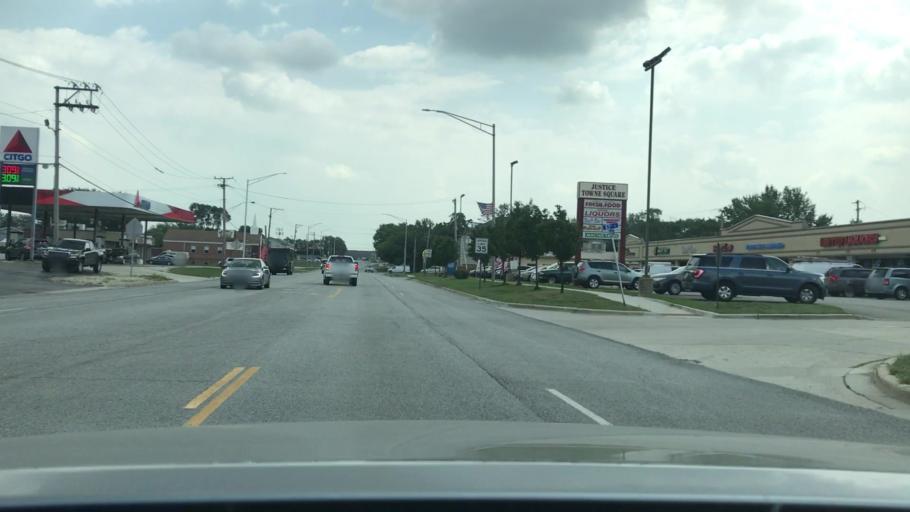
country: US
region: Illinois
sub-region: Cook County
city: Hickory Hills
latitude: 41.7396
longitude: -87.8188
